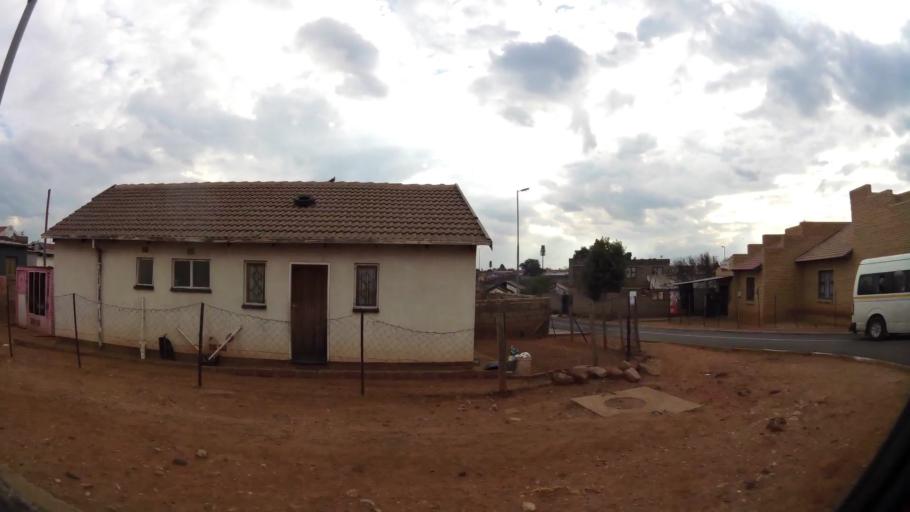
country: ZA
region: Gauteng
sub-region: City of Johannesburg Metropolitan Municipality
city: Soweto
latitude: -26.2436
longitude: 27.8122
